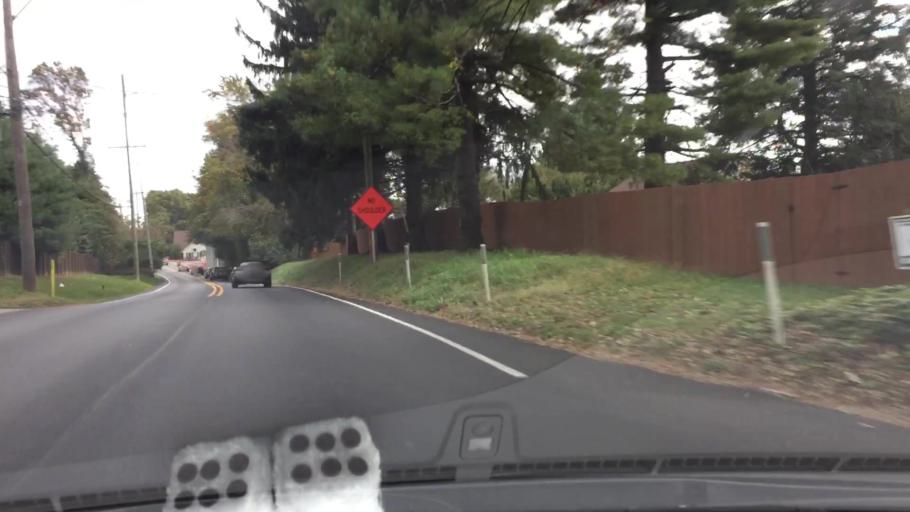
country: US
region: Pennsylvania
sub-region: Chester County
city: Malvern
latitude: 39.9718
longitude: -75.5317
